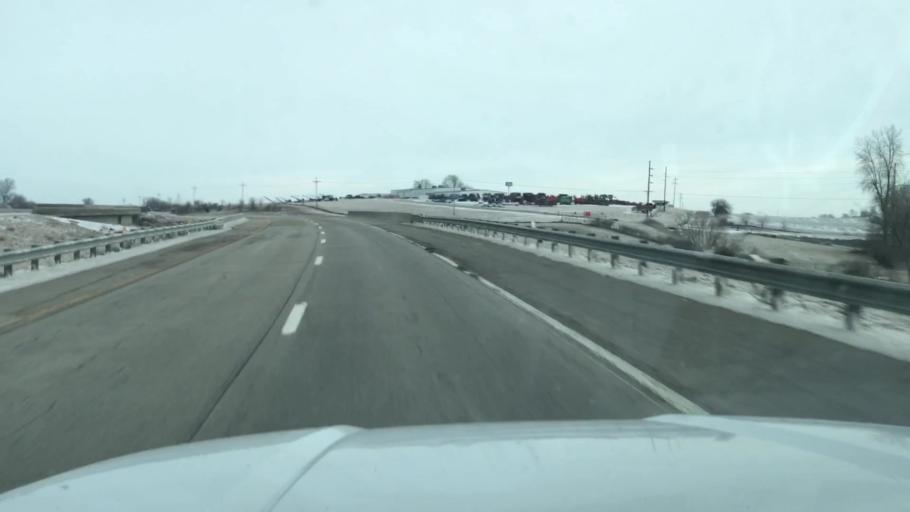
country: US
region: Missouri
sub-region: Andrew County
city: Savannah
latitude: 39.9611
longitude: -94.8609
